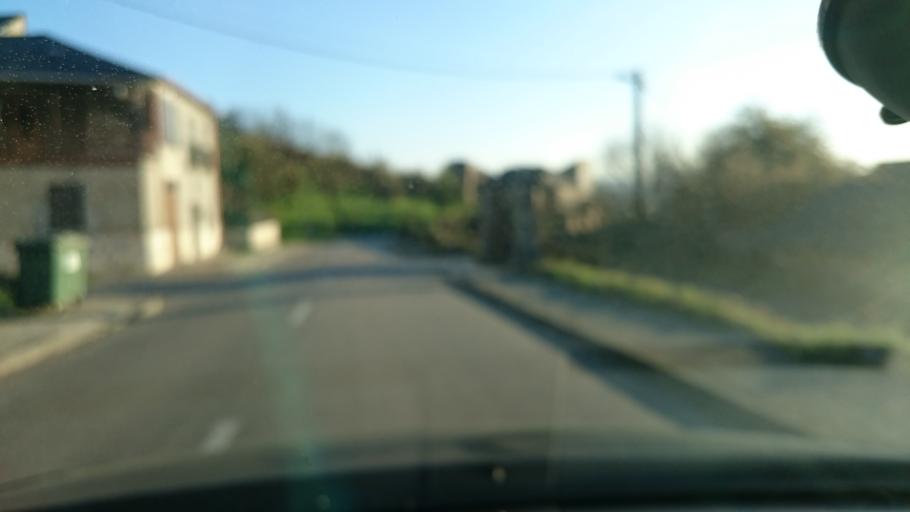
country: ES
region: Castille and Leon
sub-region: Provincia de Leon
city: Corullon
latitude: 42.5828
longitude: -6.8186
